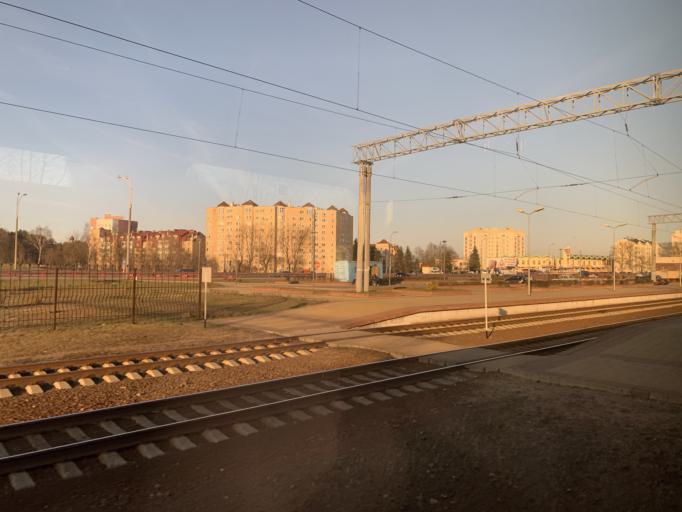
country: BY
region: Minsk
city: Zhdanovichy
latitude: 53.9480
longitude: 27.4237
